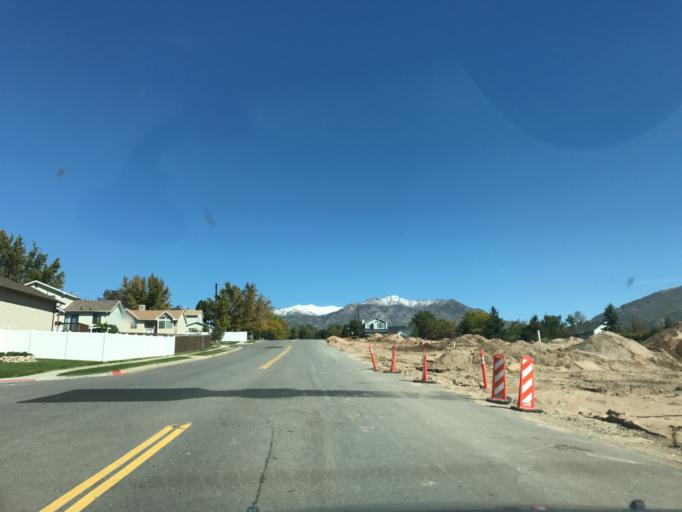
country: US
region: Utah
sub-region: Davis County
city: Hill Air Force Bace
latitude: 41.0946
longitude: -111.9413
